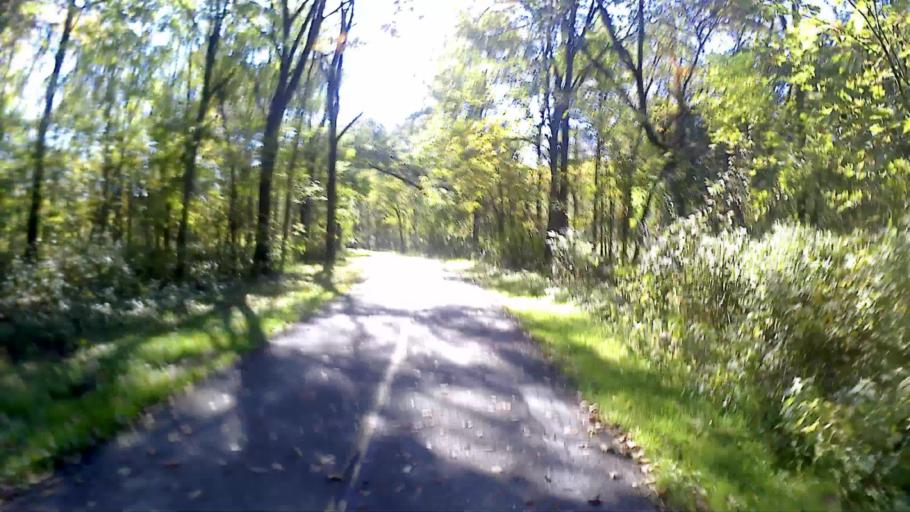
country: US
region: Illinois
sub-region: Cook County
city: Elk Grove Village
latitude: 42.0212
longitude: -87.9912
